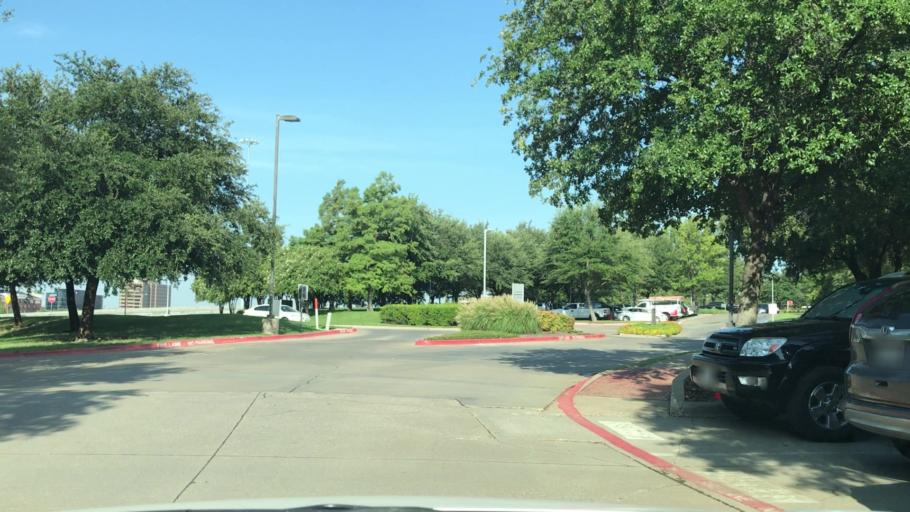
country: US
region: Texas
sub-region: Dallas County
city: Farmers Branch
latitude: 32.8944
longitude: -96.9659
